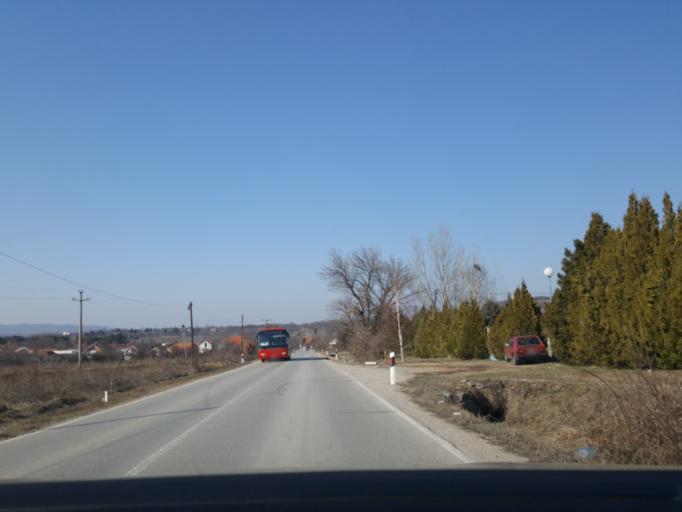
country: RS
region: Central Serbia
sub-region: Nisavski Okrug
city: Nis
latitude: 43.3944
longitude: 21.8119
